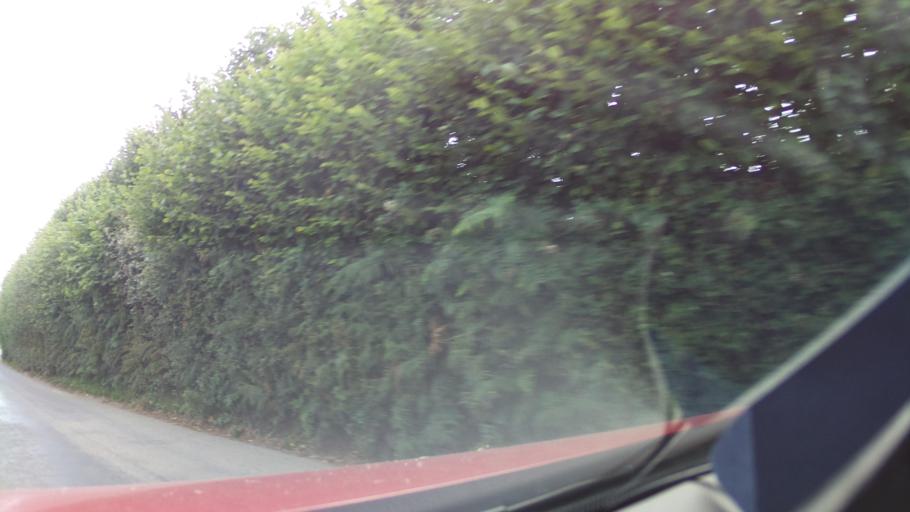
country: GB
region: England
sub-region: Devon
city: Buckfastleigh
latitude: 50.5308
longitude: -3.8249
